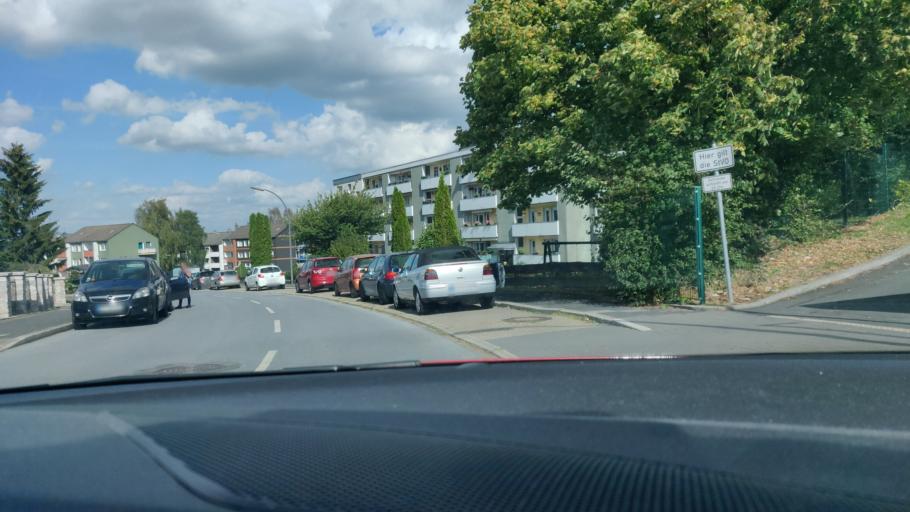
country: DE
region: North Rhine-Westphalia
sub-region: Regierungsbezirk Dusseldorf
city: Velbert
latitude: 51.3324
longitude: 7.0186
